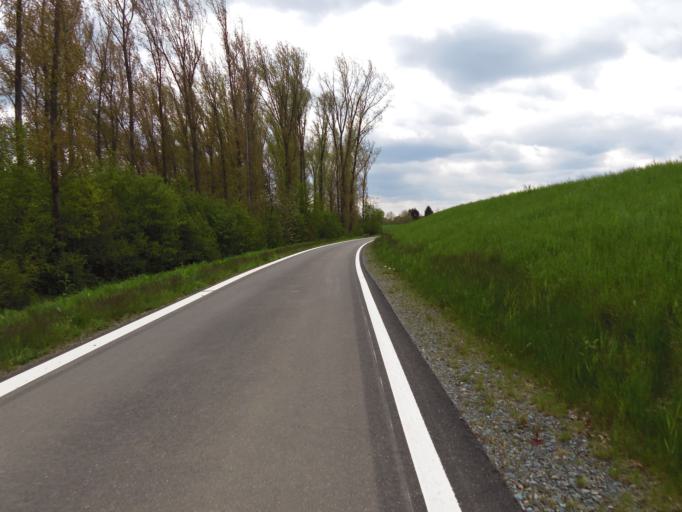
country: DE
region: Hesse
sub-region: Regierungsbezirk Darmstadt
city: Biblis
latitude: 49.6898
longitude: 8.4110
